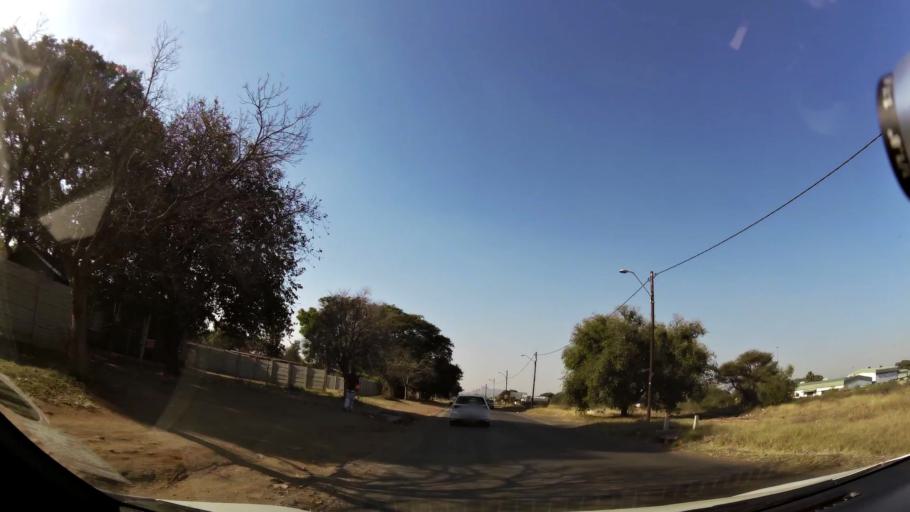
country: ZA
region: North-West
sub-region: Bojanala Platinum District Municipality
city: Rustenburg
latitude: -25.6635
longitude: 27.2616
